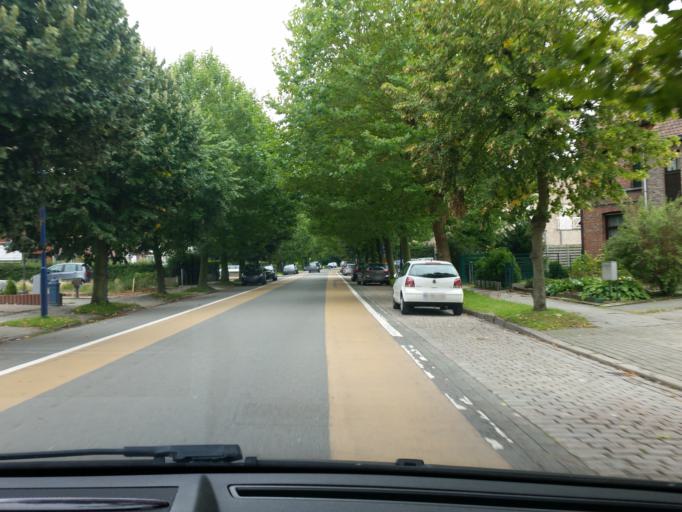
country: BE
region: Flanders
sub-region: Provincie Antwerpen
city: Kontich
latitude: 51.1273
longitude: 4.4483
